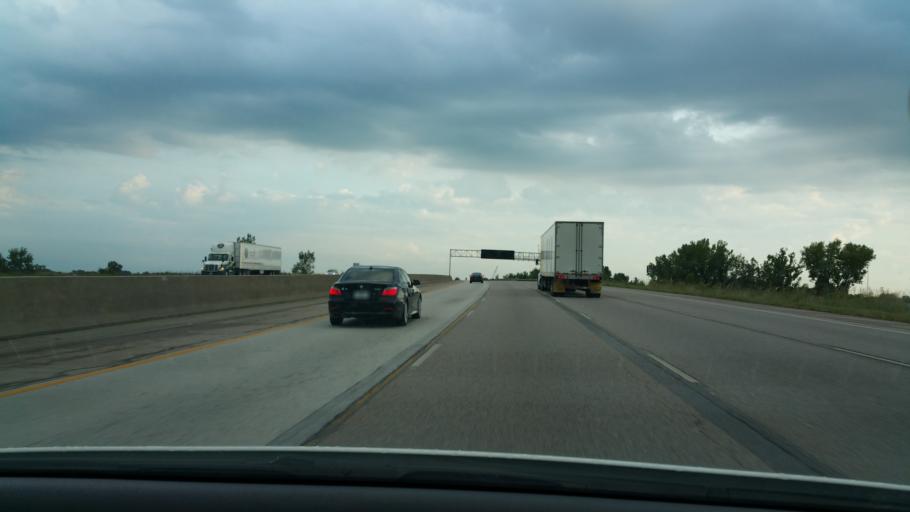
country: US
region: Iowa
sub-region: Polk County
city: Saylorville
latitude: 41.6721
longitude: -93.5781
